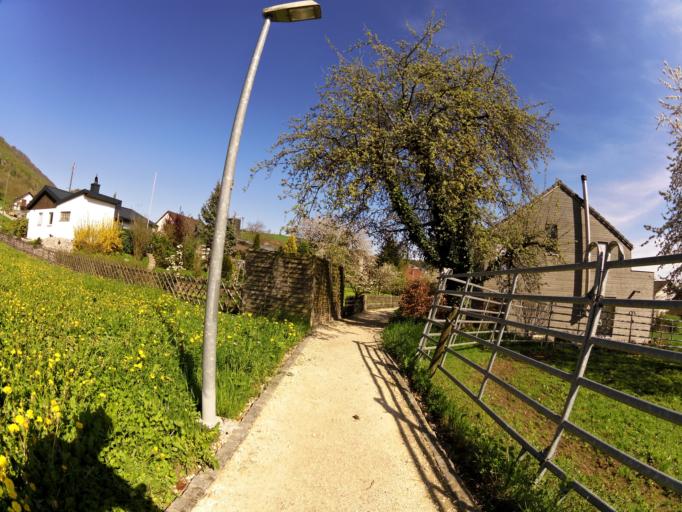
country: CH
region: Solothurn
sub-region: Bezirk Goesgen
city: Niedererlinsbach
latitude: 47.4099
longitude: 8.0037
